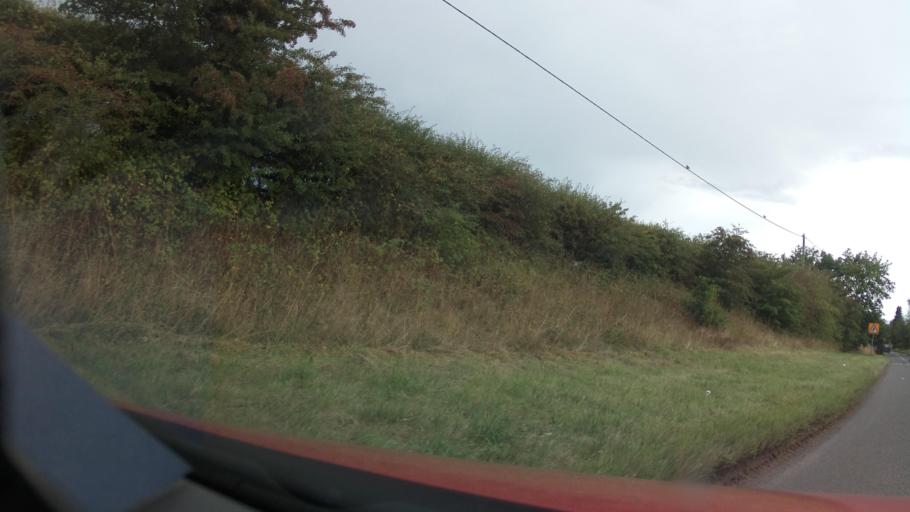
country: GB
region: England
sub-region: Shropshire
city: Woodcote
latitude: 52.7254
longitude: -2.3493
